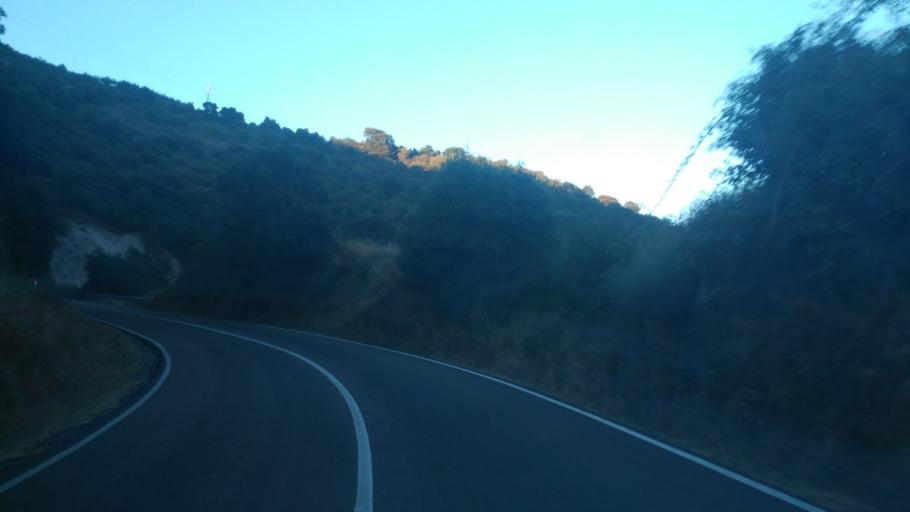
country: ES
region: Castille and Leon
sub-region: Provincia de Salamanca
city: Mieza
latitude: 41.1848
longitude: -6.6627
